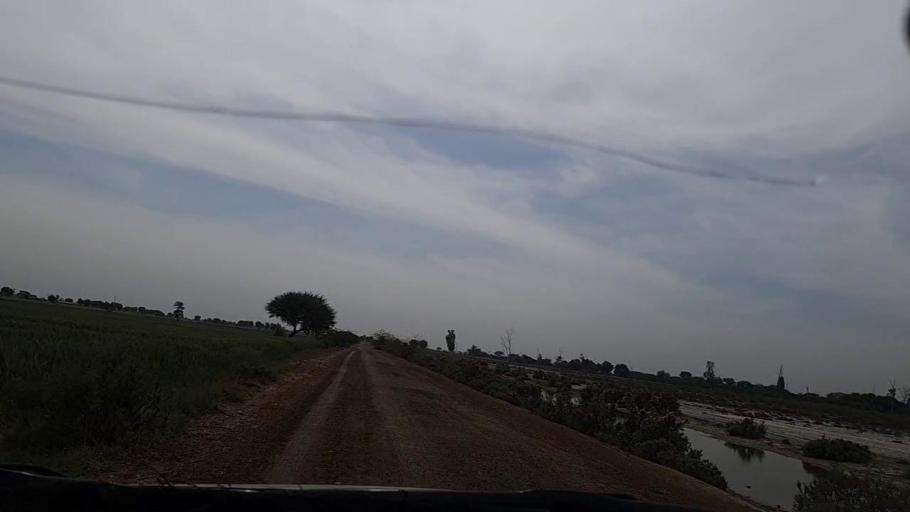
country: PK
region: Sindh
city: Dhoro Naro
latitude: 25.4457
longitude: 69.4921
